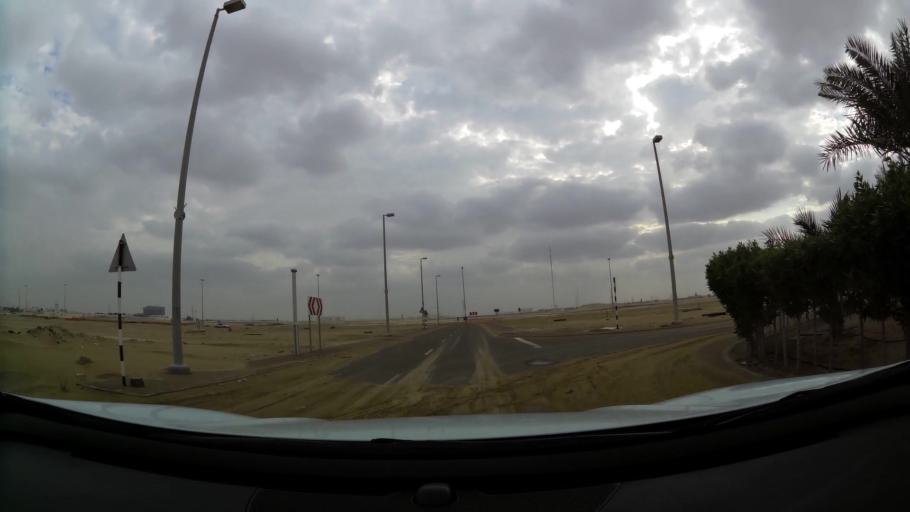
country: AE
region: Abu Dhabi
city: Abu Dhabi
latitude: 24.3461
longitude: 54.6115
